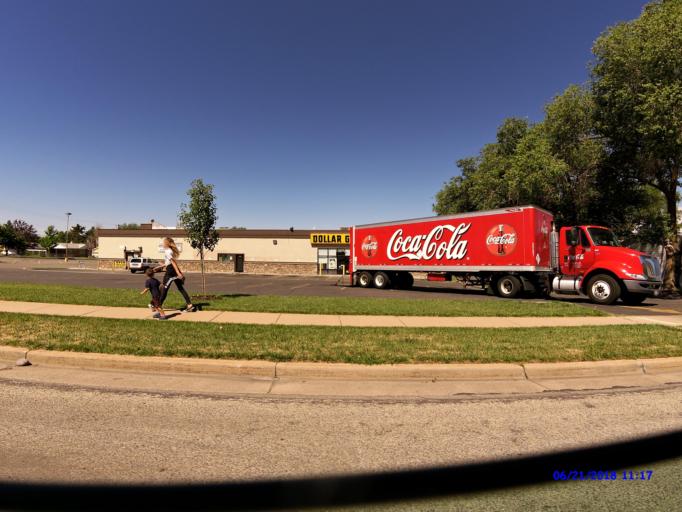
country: US
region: Utah
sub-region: Weber County
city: Ogden
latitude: 41.2523
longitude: -111.9543
